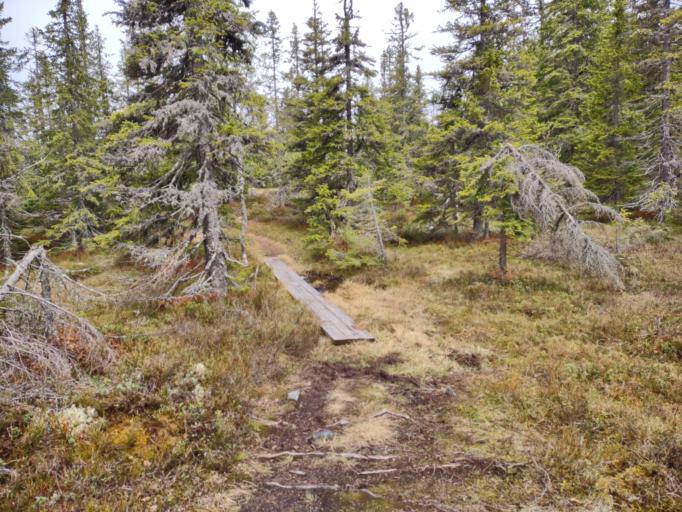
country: NO
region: Oppland
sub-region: Gran
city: Jaren
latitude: 60.4263
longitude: 10.6860
